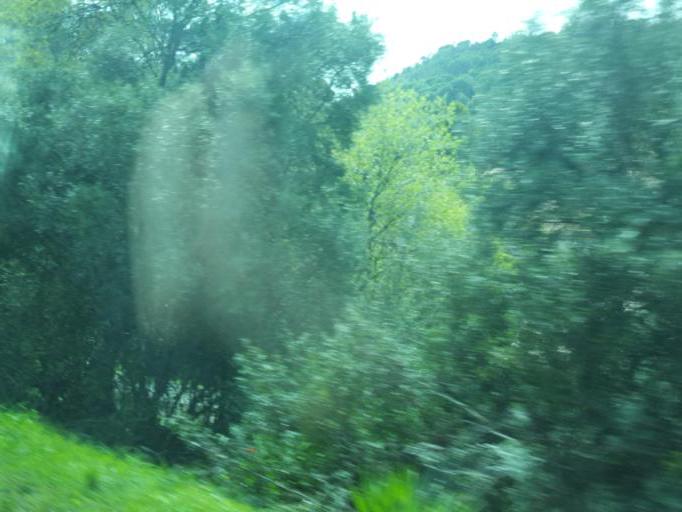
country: PT
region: Faro
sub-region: Monchique
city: Monchique
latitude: 37.2867
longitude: -8.5522
